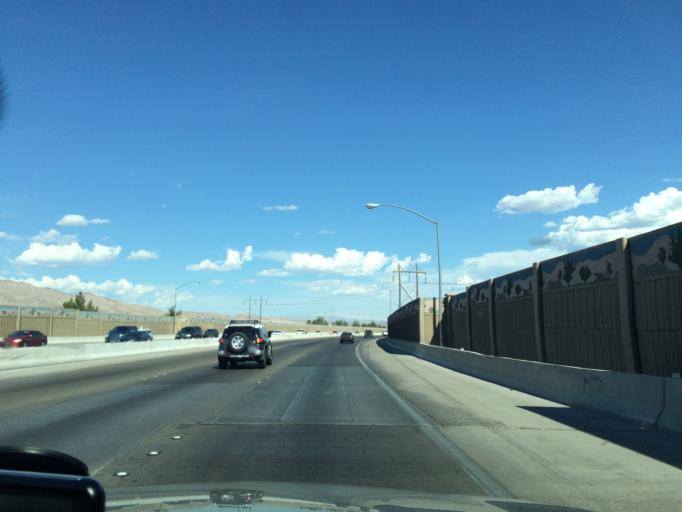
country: US
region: Nevada
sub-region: Clark County
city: North Las Vegas
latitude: 36.1666
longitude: -115.0983
